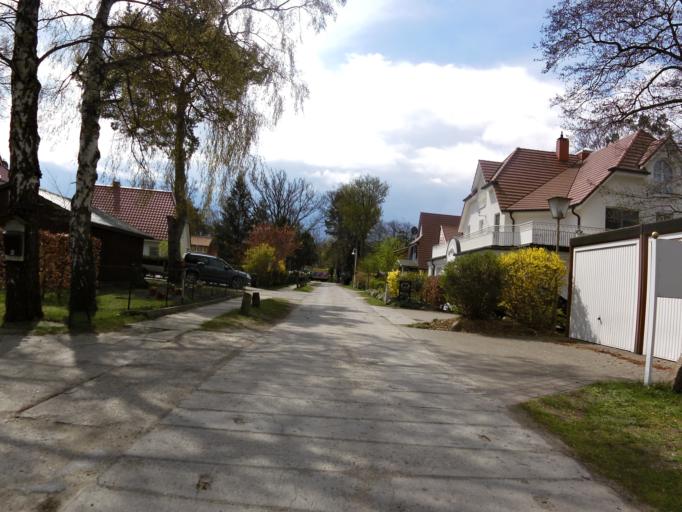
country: DE
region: Mecklenburg-Vorpommern
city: Ostseebad Prerow
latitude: 54.4487
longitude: 12.5617
